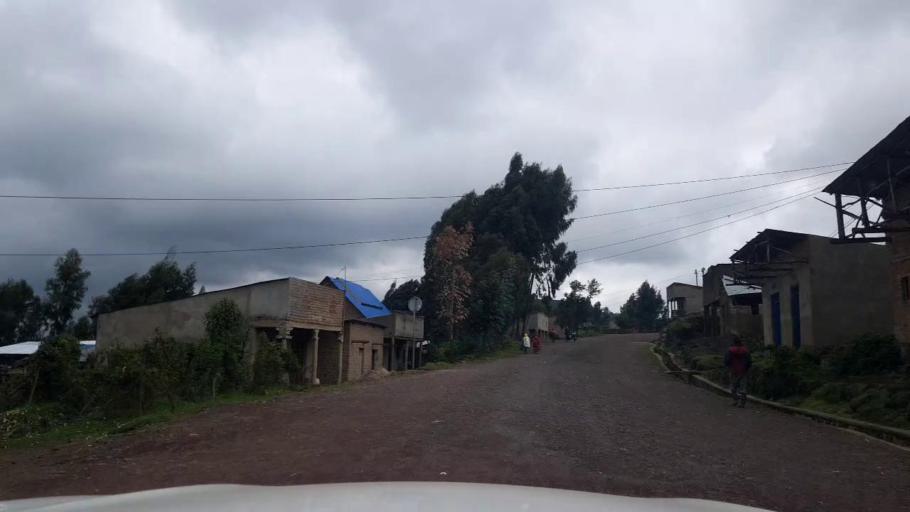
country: RW
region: Northern Province
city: Musanze
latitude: -1.5831
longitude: 29.4746
